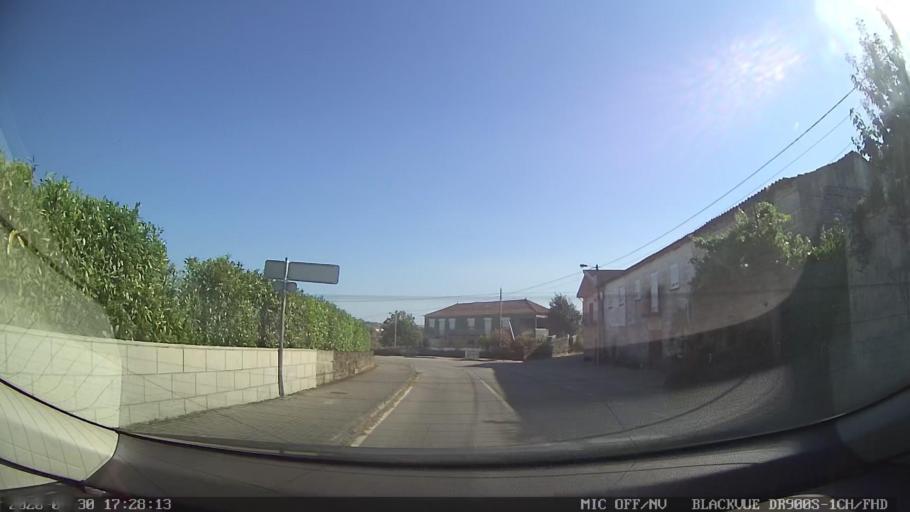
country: PT
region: Vila Real
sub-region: Murca
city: Murca
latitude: 41.3277
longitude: -7.4661
